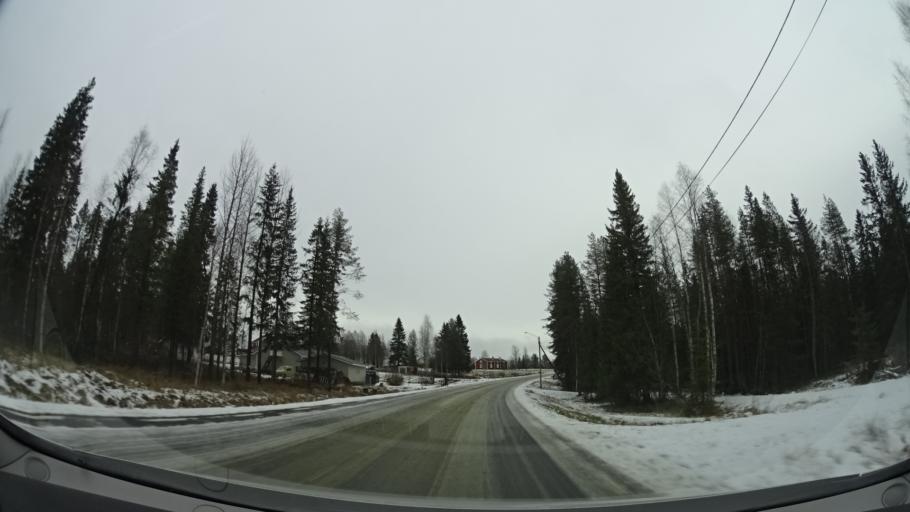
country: SE
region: Vaesterbotten
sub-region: Lycksele Kommun
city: Lycksele
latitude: 64.5191
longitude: 18.3987
